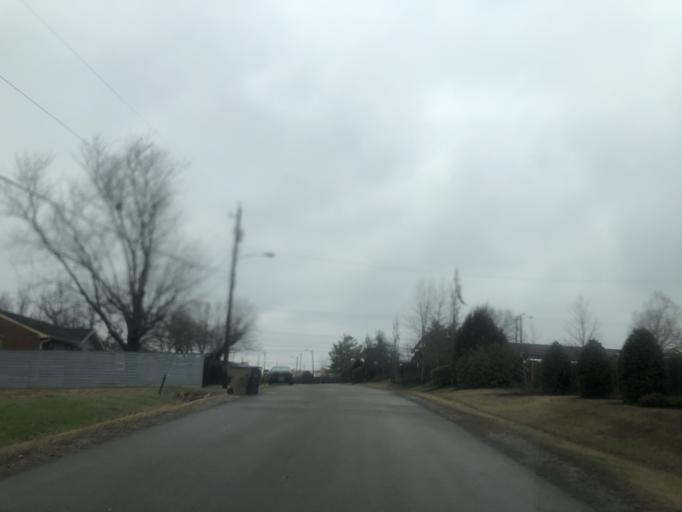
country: US
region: Tennessee
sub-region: Davidson County
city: Lakewood
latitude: 36.1440
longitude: -86.6700
